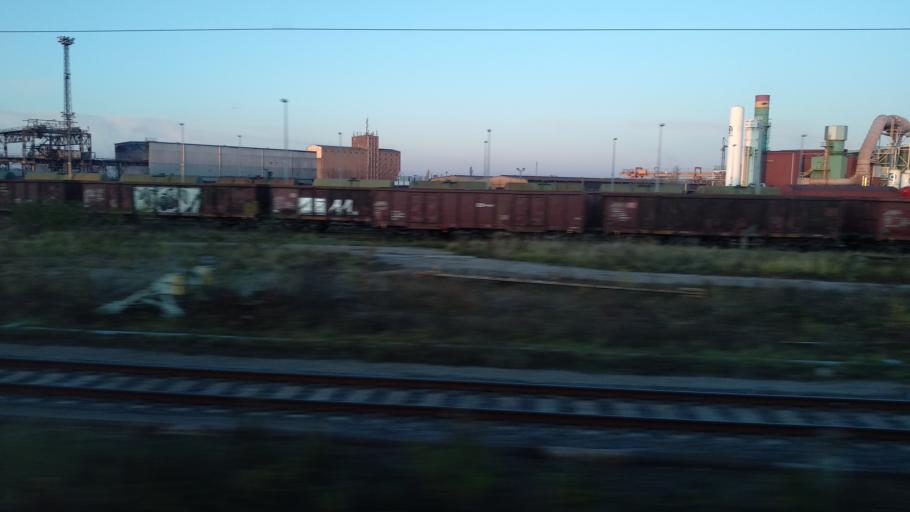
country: DE
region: Saxony
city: Riesa
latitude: 51.3113
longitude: 13.2713
